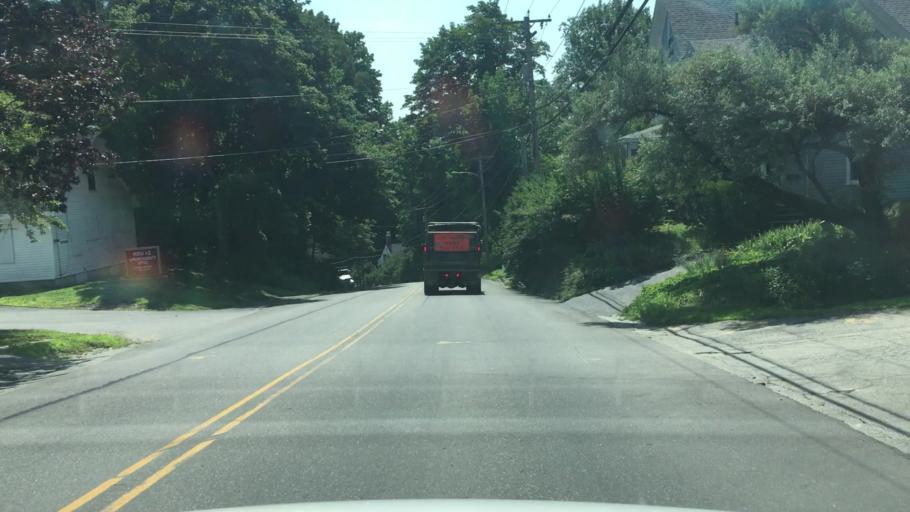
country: US
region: Maine
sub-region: Kennebec County
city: Hallowell
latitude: 44.2900
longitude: -69.7965
